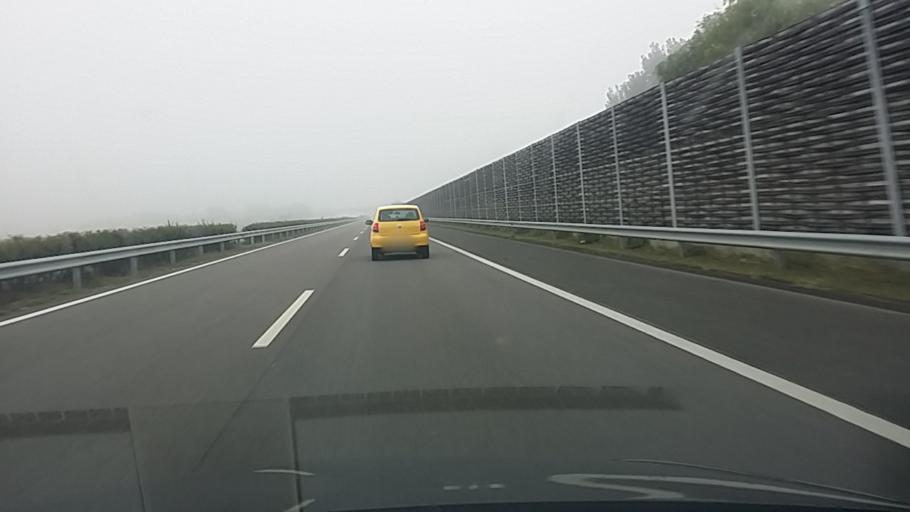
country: HU
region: Csongrad
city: Domaszek
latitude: 46.2649
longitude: 20.0390
